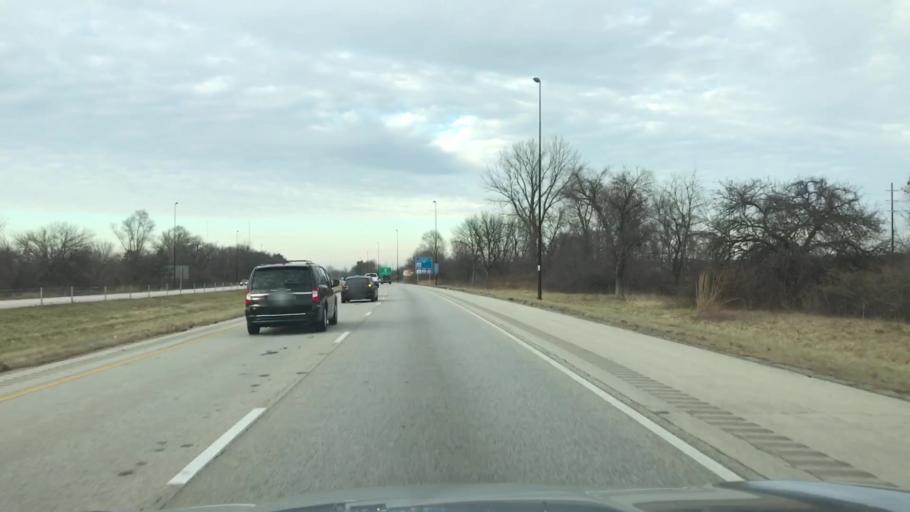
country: US
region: Illinois
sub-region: Sangamon County
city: Grandview
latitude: 39.8095
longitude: -89.5931
